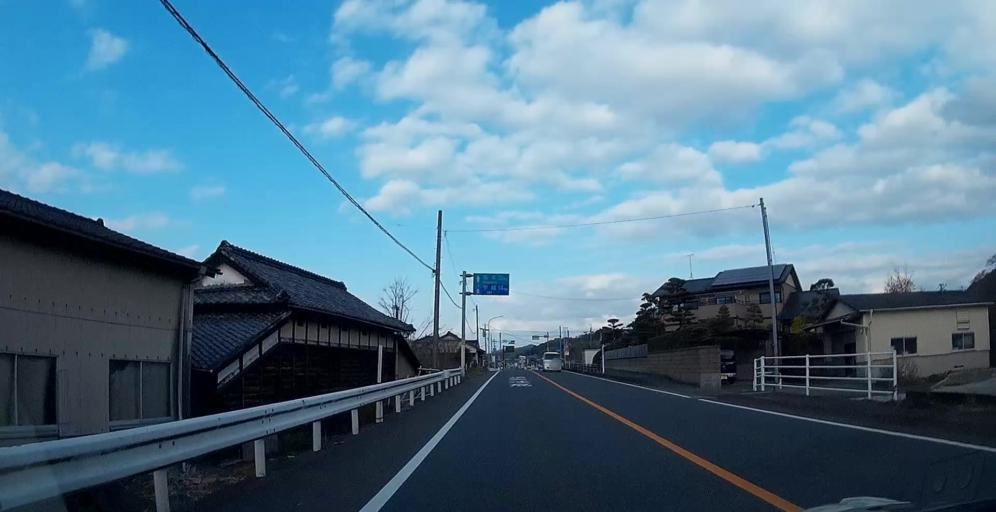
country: JP
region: Kumamoto
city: Yatsushiro
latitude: 32.5416
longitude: 130.6736
